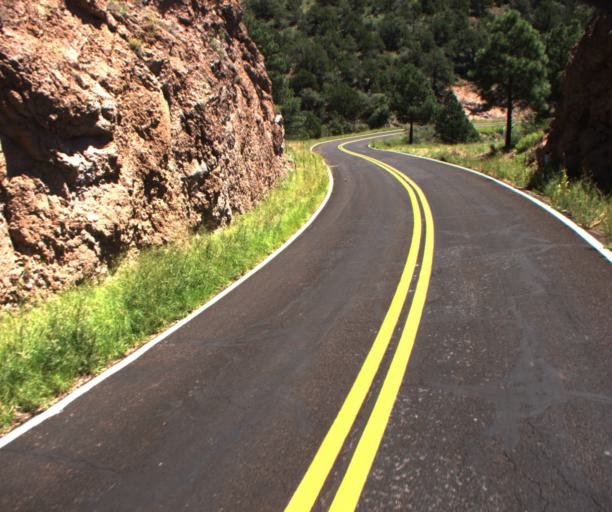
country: US
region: Arizona
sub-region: Greenlee County
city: Morenci
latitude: 33.4143
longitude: -109.3628
